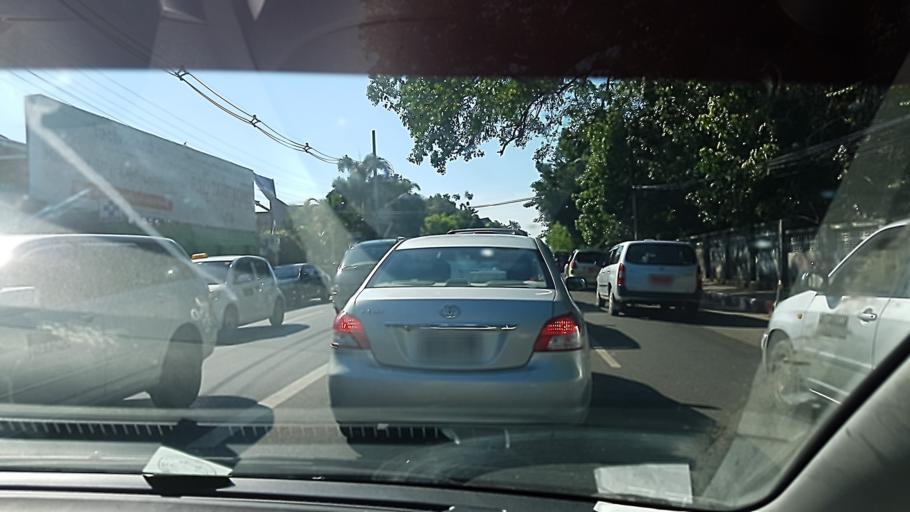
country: MM
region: Yangon
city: Yangon
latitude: 16.8280
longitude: 96.1395
